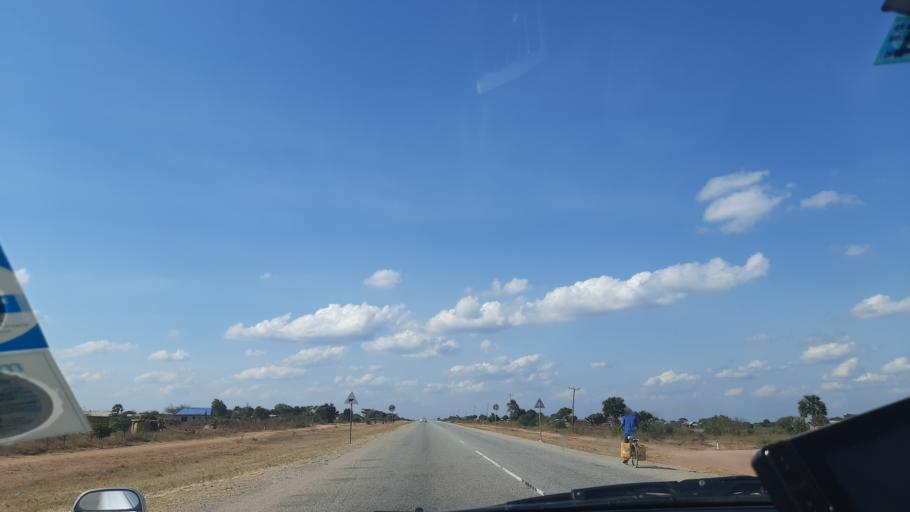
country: TZ
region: Singida
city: Itigi
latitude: -5.5434
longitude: 34.6706
